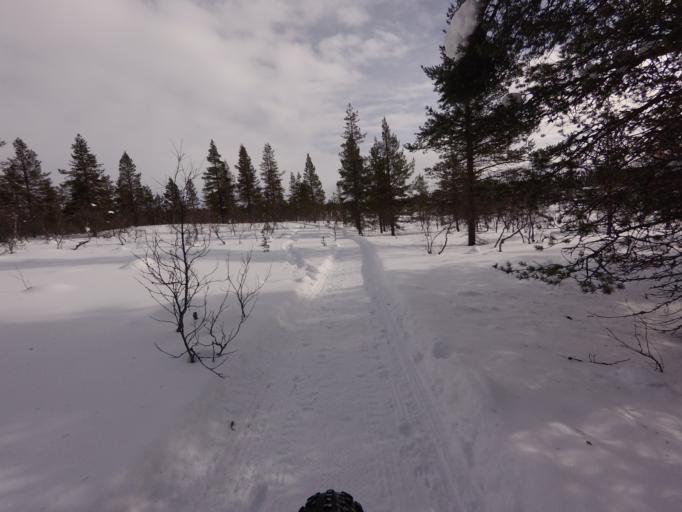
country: FI
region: Lapland
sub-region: Pohjois-Lappi
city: Ivalo
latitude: 68.3469
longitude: 27.4491
